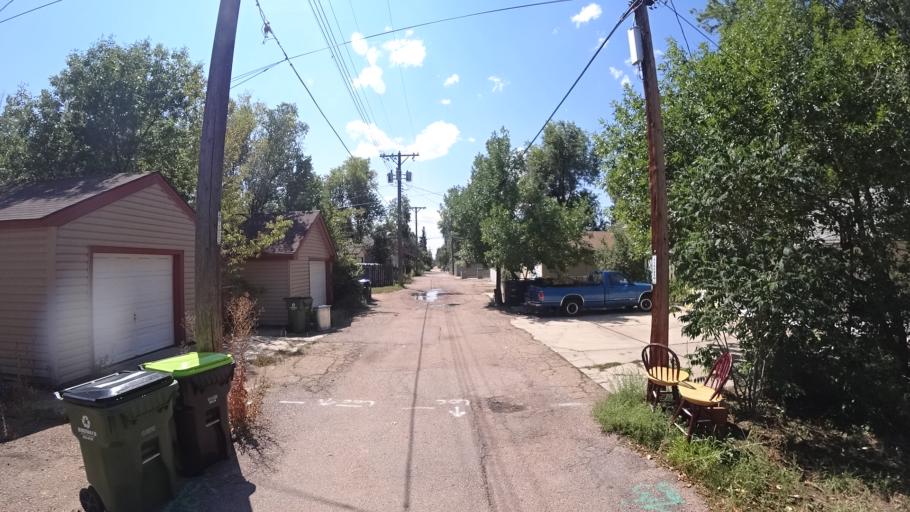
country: US
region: Colorado
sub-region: El Paso County
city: Colorado Springs
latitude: 38.8613
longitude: -104.8157
